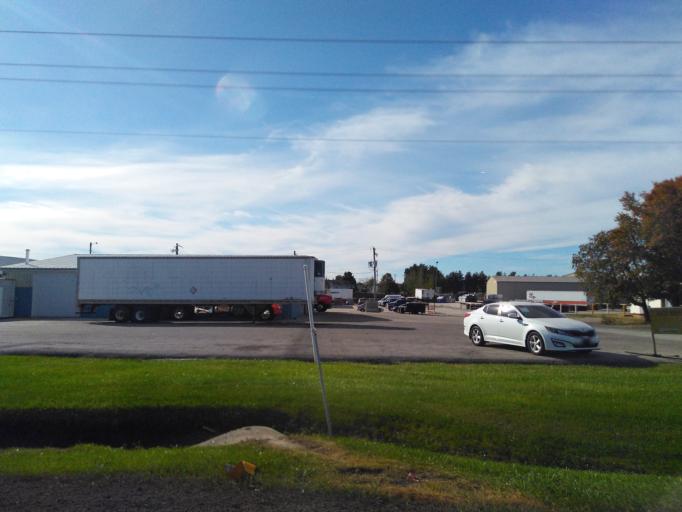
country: US
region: Illinois
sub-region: Madison County
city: Troy
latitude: 38.7176
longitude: -89.8877
